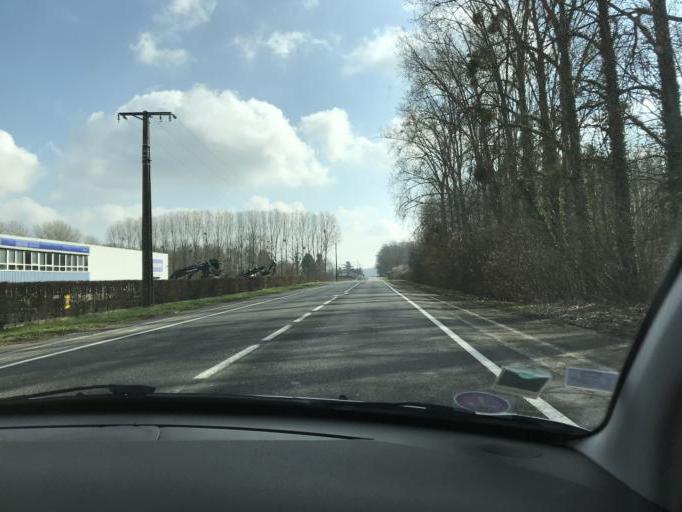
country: FR
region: Picardie
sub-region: Departement de l'Aisne
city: Villeneuve-Saint-Germain
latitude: 49.3670
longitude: 3.3700
